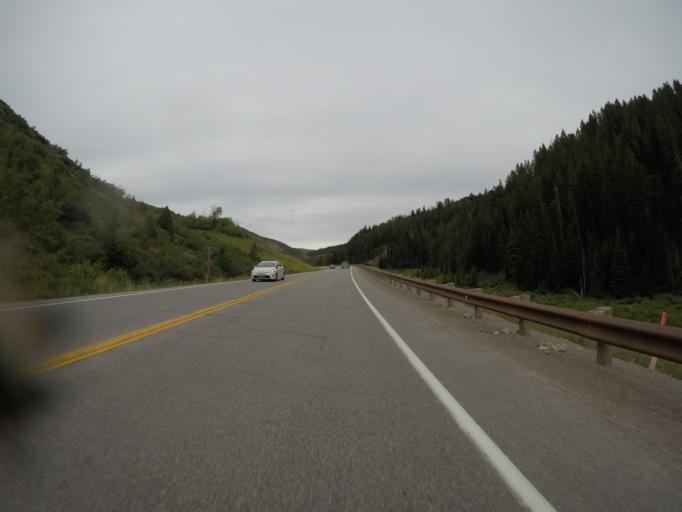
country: US
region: Wyoming
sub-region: Lincoln County
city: Afton
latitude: 42.4885
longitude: -110.9472
